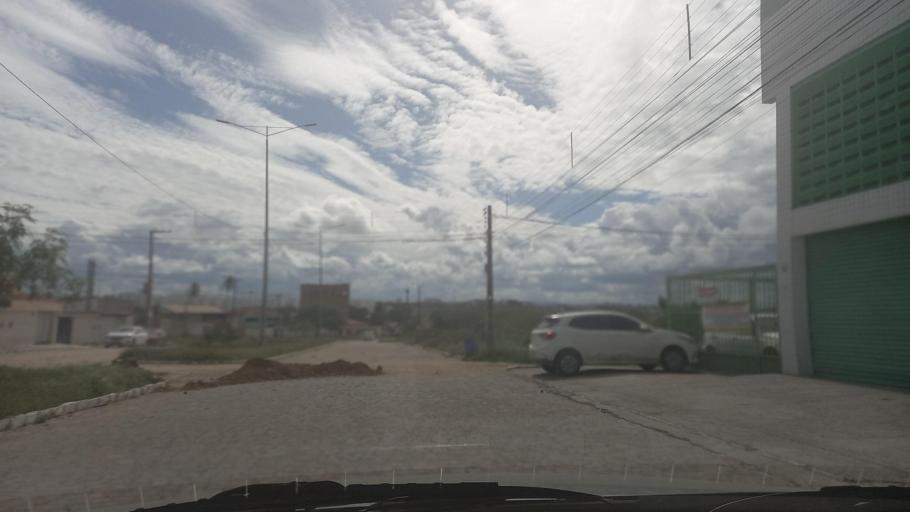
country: BR
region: Pernambuco
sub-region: Caruaru
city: Caruaru
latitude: -8.2911
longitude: -35.9907
